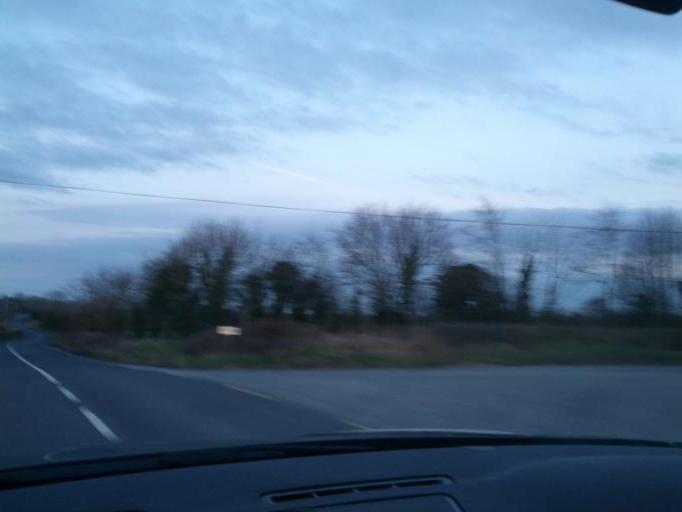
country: IE
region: Leinster
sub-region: Uibh Fhaili
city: Banagher
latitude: 53.0888
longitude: -8.0459
